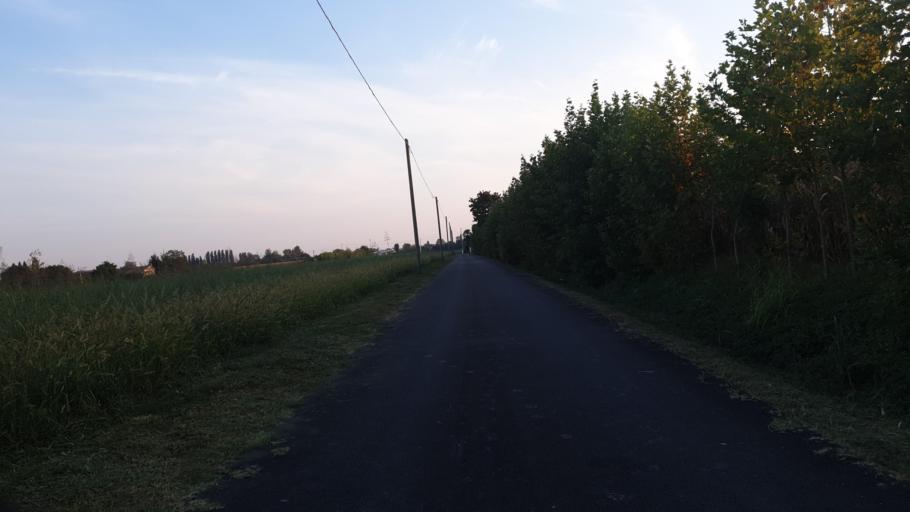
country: IT
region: Veneto
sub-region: Provincia di Padova
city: Albignasego
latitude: 45.3608
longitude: 11.8786
